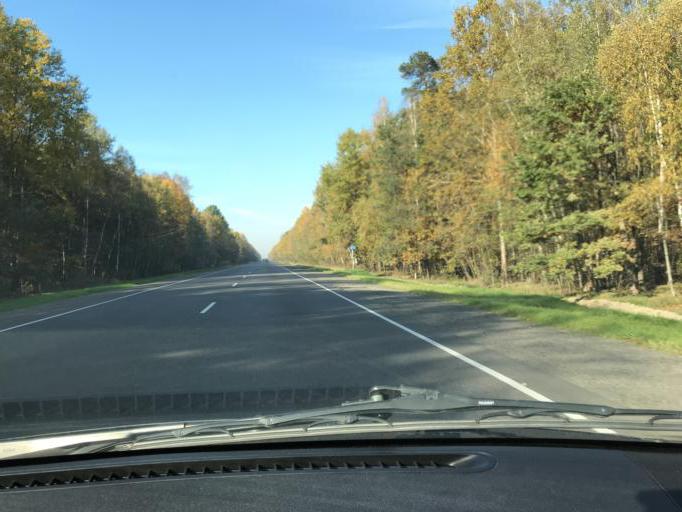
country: BY
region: Brest
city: Horad Luninyets
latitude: 52.3044
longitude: 26.7023
